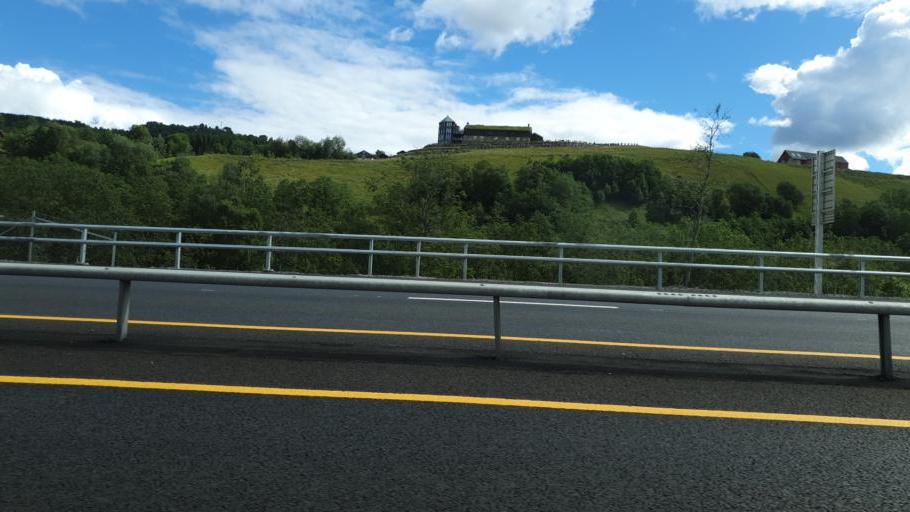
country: NO
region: Sor-Trondelag
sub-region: Midtre Gauldal
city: Storen
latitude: 62.9411
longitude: 10.1915
